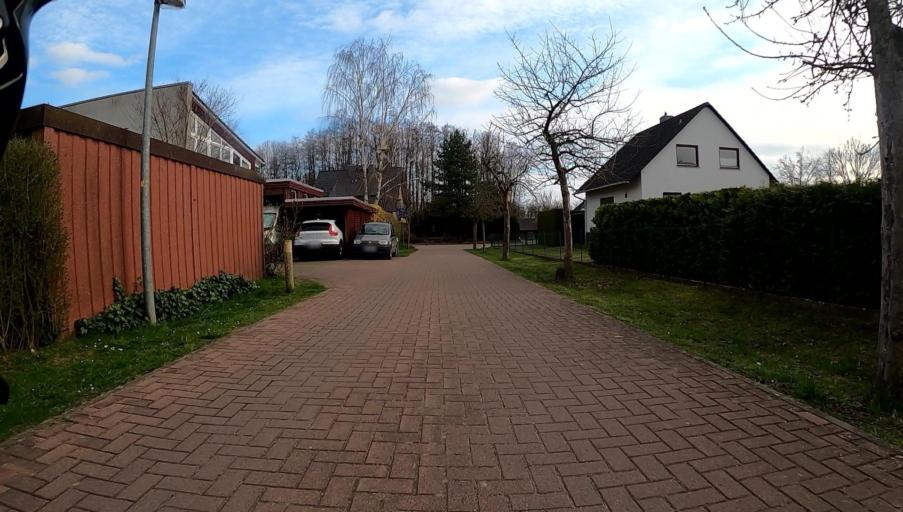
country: DE
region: Lower Saxony
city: Lindwedel
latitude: 52.5556
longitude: 9.6356
